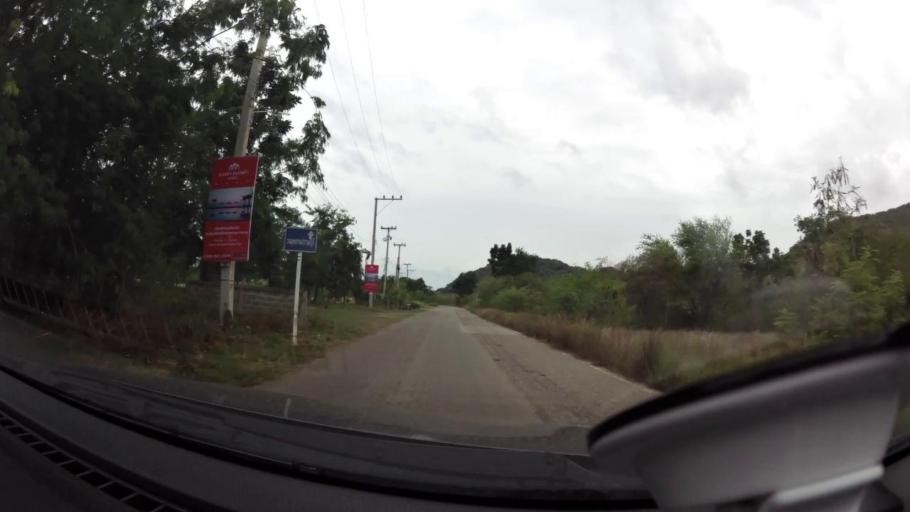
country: TH
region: Prachuap Khiri Khan
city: Pran Buri
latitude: 12.4246
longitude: 99.9793
